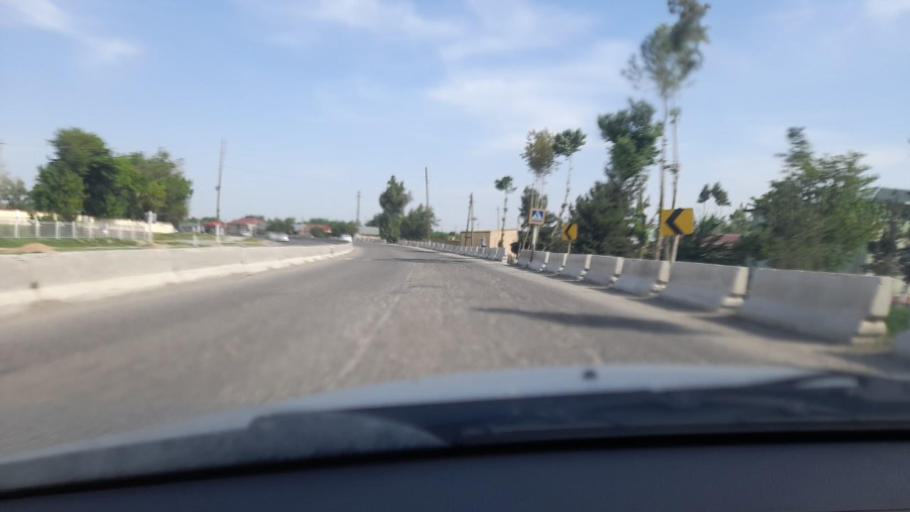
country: UZ
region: Samarqand
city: Daxbet
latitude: 39.7657
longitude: 66.9022
